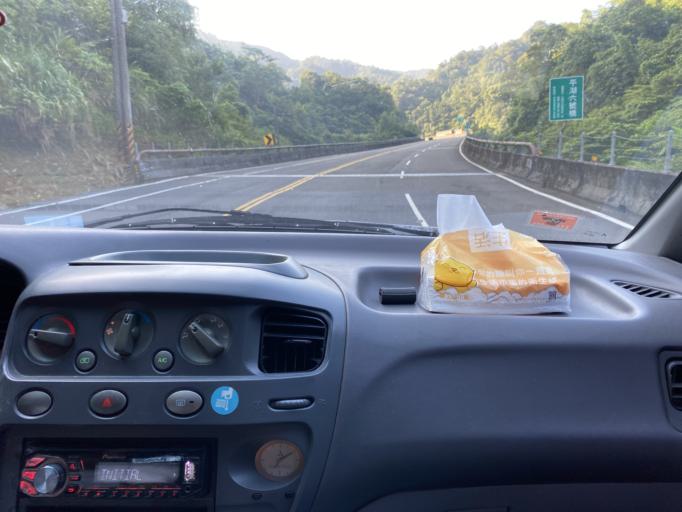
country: TW
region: Taiwan
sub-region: Keelung
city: Keelung
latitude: 25.0283
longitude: 121.7805
